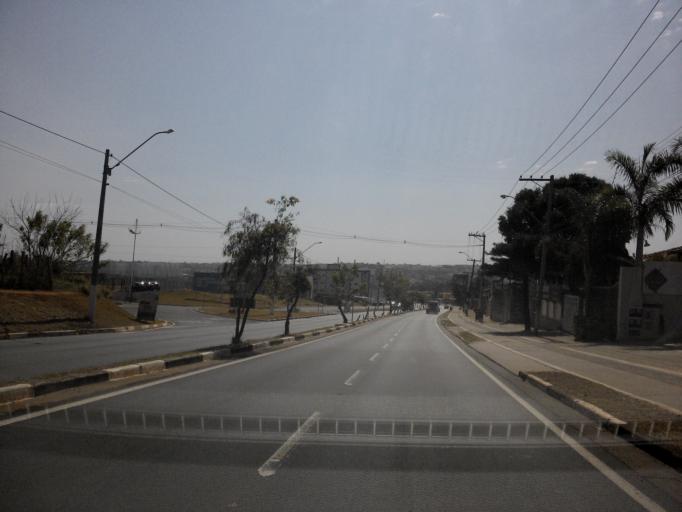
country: BR
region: Sao Paulo
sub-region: Hortolandia
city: Hortolandia
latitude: -22.8732
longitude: -47.2278
